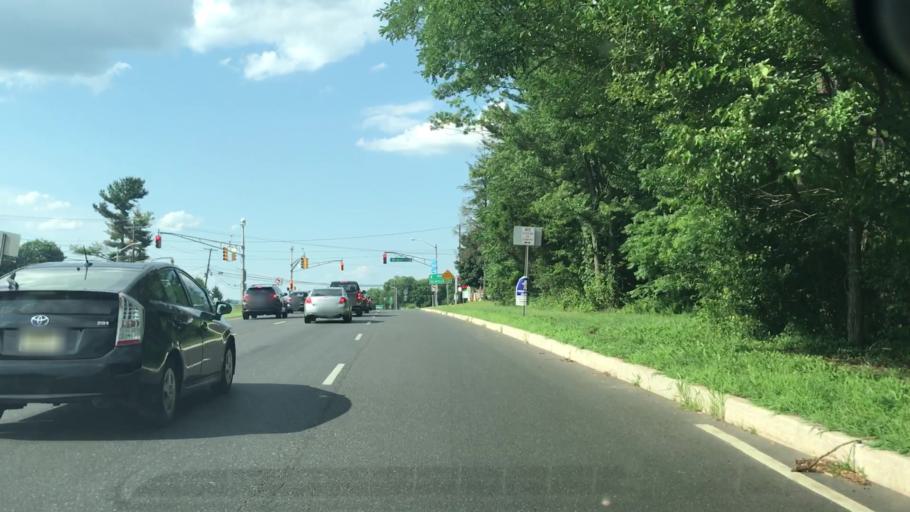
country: US
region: New Jersey
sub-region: Hunterdon County
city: Flemington
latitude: 40.4394
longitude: -74.8581
